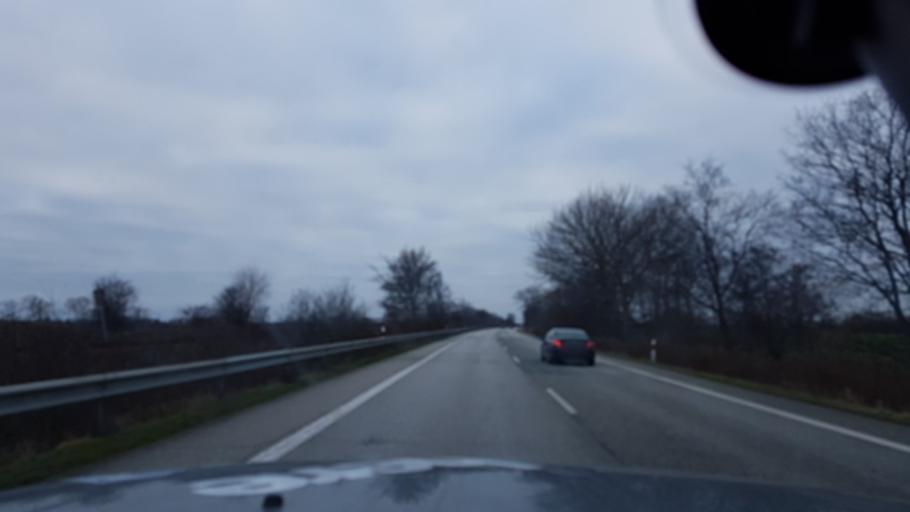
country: DE
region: Schleswig-Holstein
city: Fehmarn
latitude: 54.4592
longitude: 11.1939
